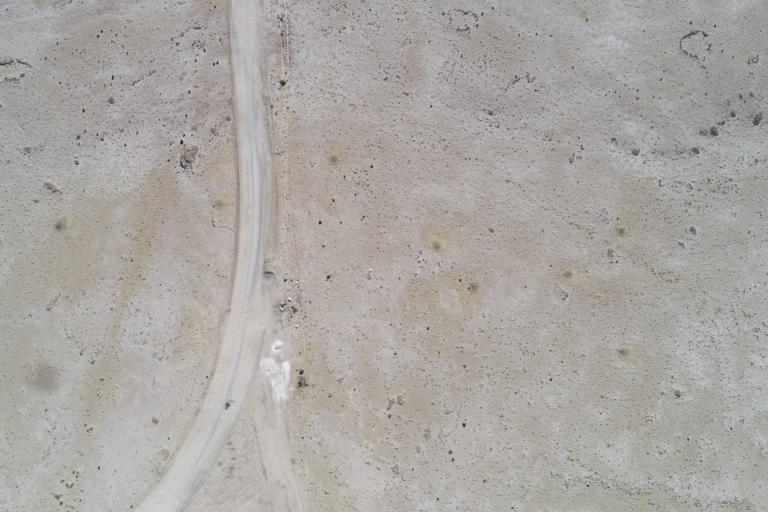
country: BO
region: Potosi
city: Colchani
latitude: -20.3528
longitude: -66.9028
